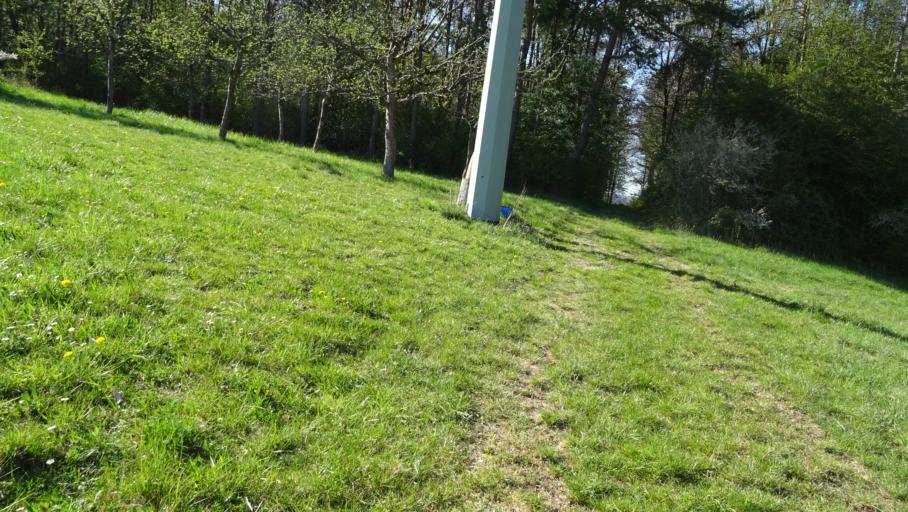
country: DE
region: Baden-Wuerttemberg
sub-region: Karlsruhe Region
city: Billigheim
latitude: 49.4037
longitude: 9.2511
